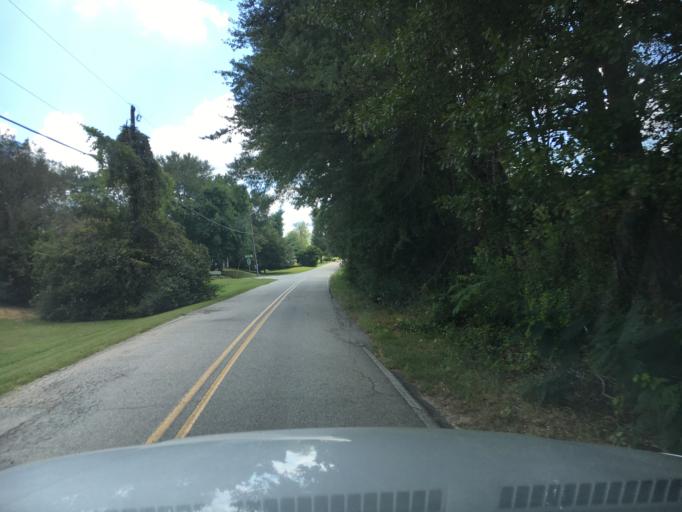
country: US
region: South Carolina
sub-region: Spartanburg County
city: Wellford
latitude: 34.8859
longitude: -82.0591
